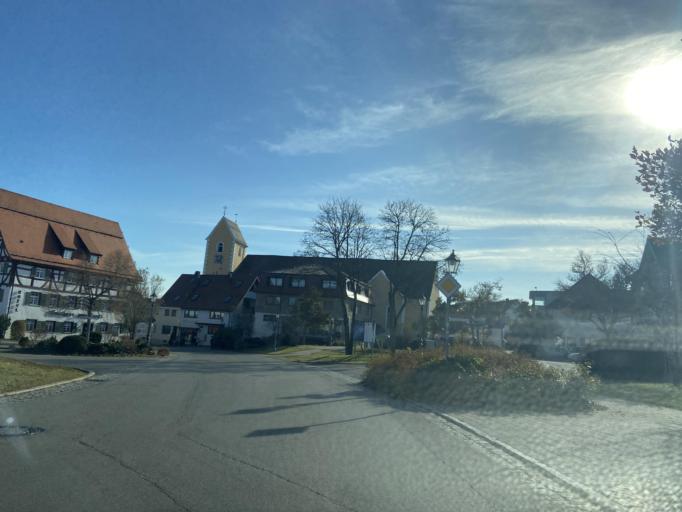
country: DE
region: Baden-Wuerttemberg
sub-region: Tuebingen Region
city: Stetten am Kalten Markt
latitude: 48.1210
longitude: 9.0781
